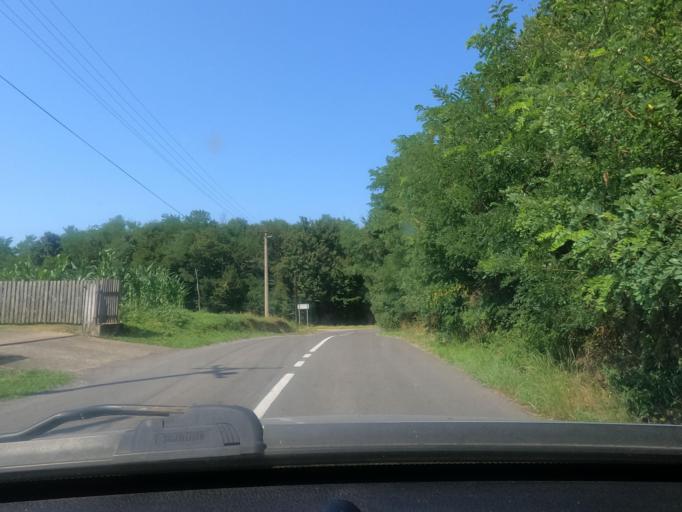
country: RS
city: Kozjak
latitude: 44.5495
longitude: 19.2929
